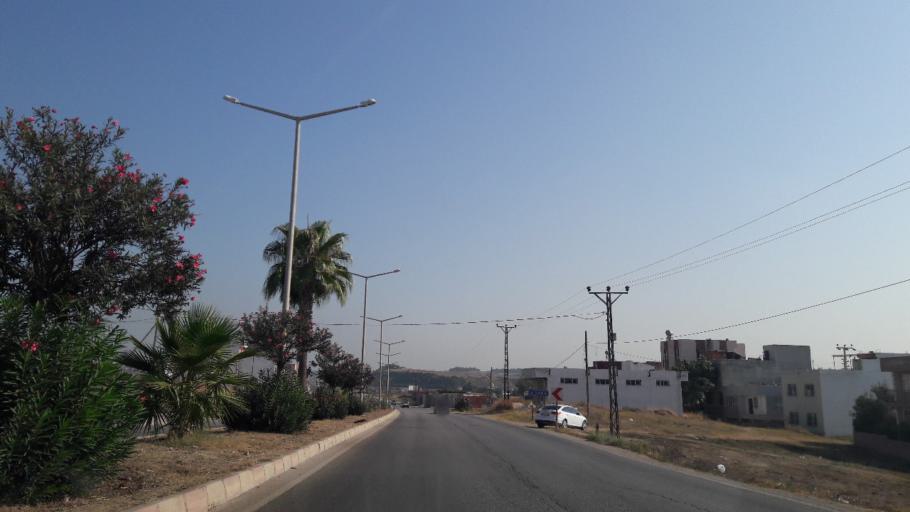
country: TR
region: Adana
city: Yuregir
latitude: 37.0461
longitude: 35.4355
